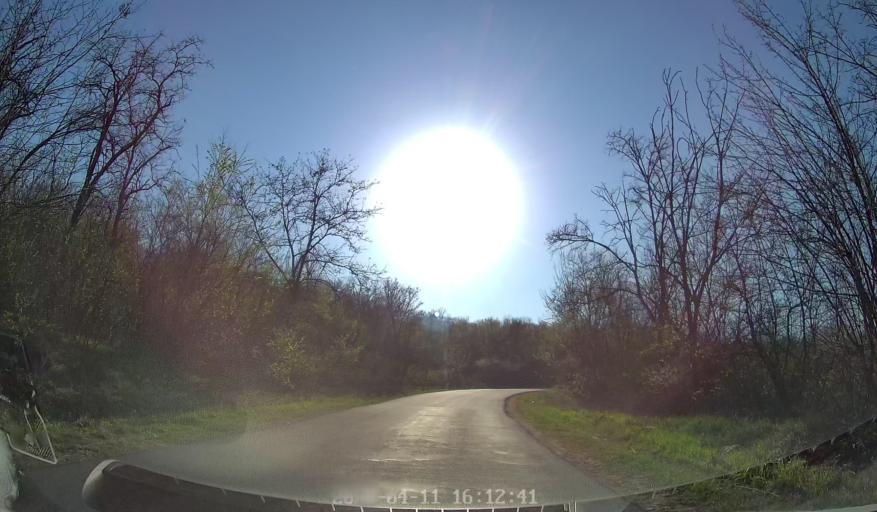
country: MD
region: Chisinau
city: Vadul lui Voda
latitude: 47.0700
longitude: 29.1191
